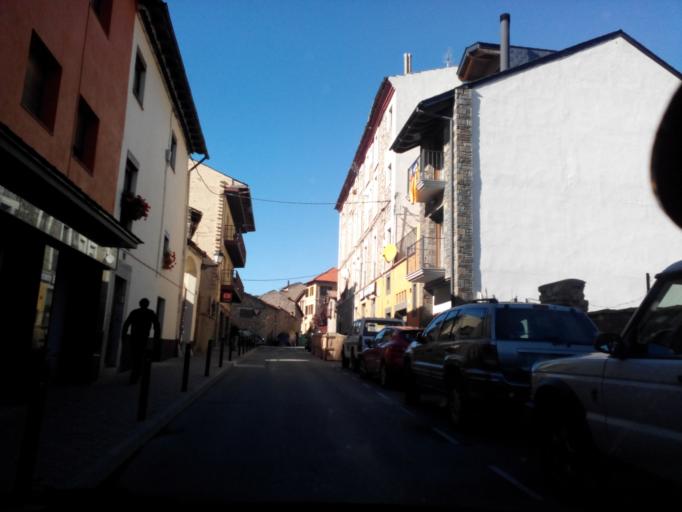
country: ES
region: Catalonia
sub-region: Provincia de Lleida
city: Bellver de Cerdanya
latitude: 42.3699
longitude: 1.7761
